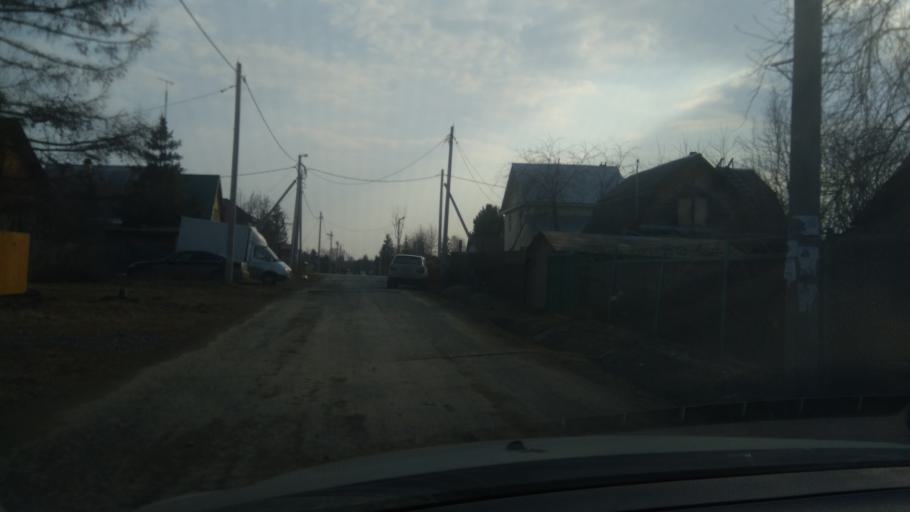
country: RU
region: Sverdlovsk
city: Severka
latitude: 56.8524
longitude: 60.3853
